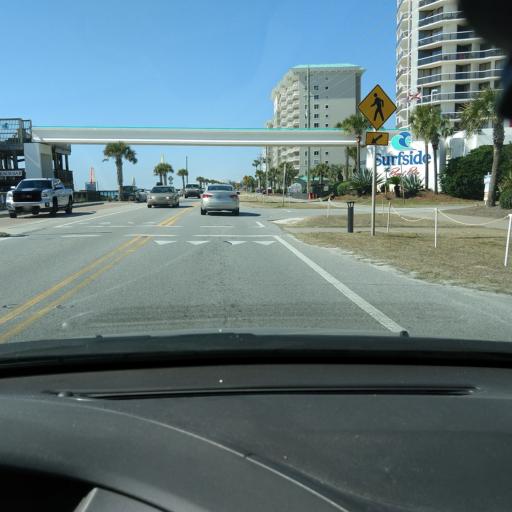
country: US
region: Florida
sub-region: Walton County
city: Miramar Beach
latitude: 30.3753
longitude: -86.3658
